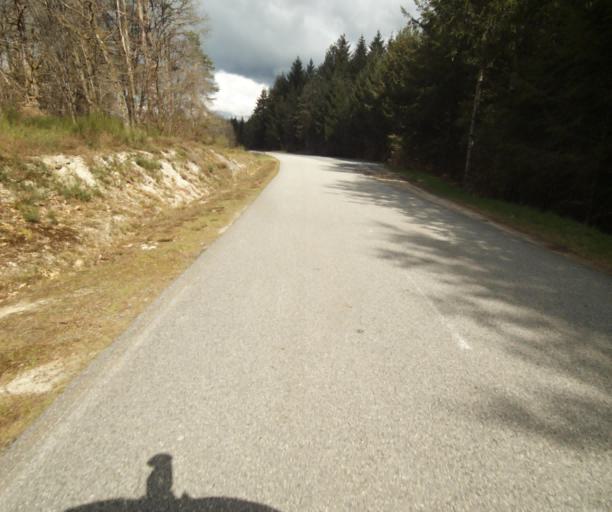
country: FR
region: Limousin
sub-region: Departement de la Correze
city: Correze
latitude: 45.2952
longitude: 1.8955
